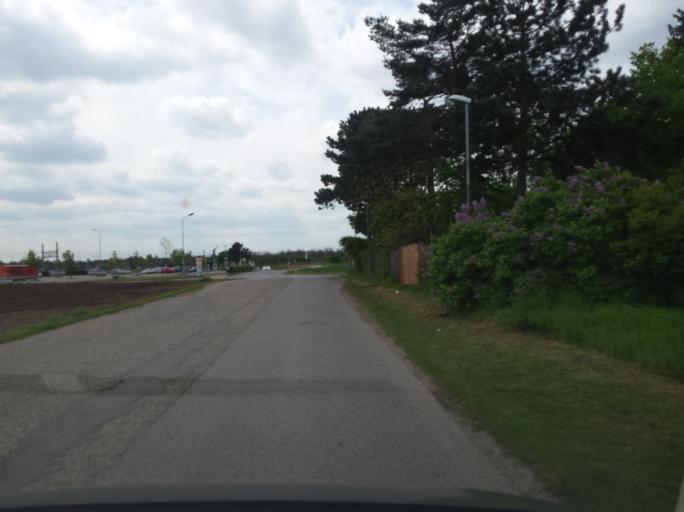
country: AT
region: Lower Austria
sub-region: Politischer Bezirk Ganserndorf
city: Parbasdorf
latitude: 48.3120
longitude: 16.5980
